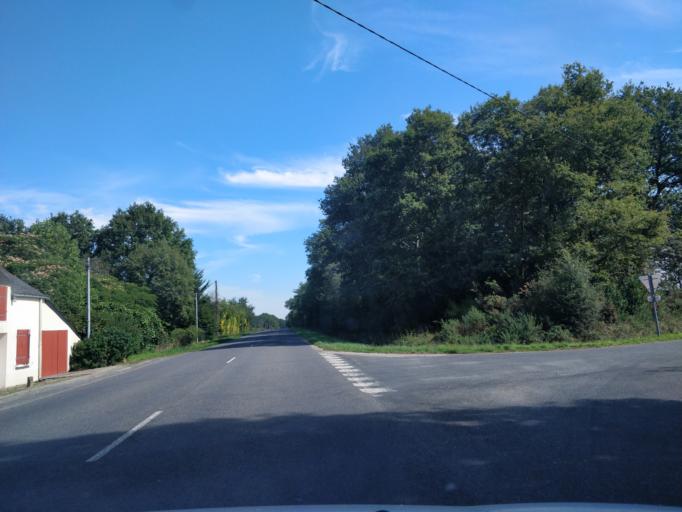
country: FR
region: Pays de la Loire
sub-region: Departement de la Loire-Atlantique
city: Quilly
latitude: 47.4745
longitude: -1.9196
